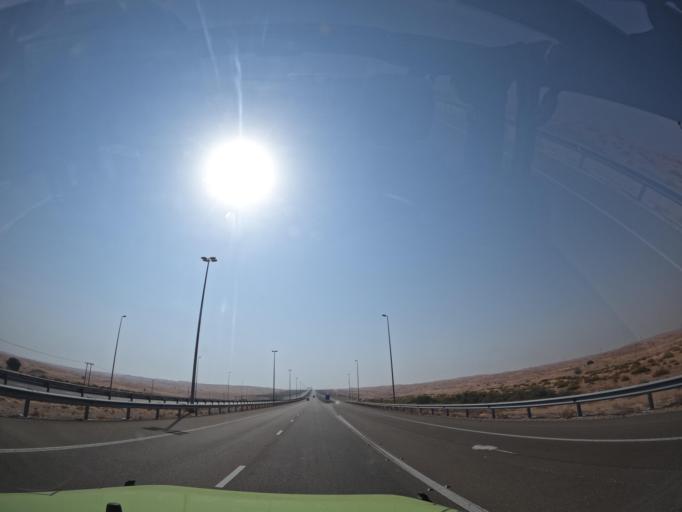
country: OM
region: Al Buraimi
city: Al Buraymi
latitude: 24.4409
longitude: 55.6646
